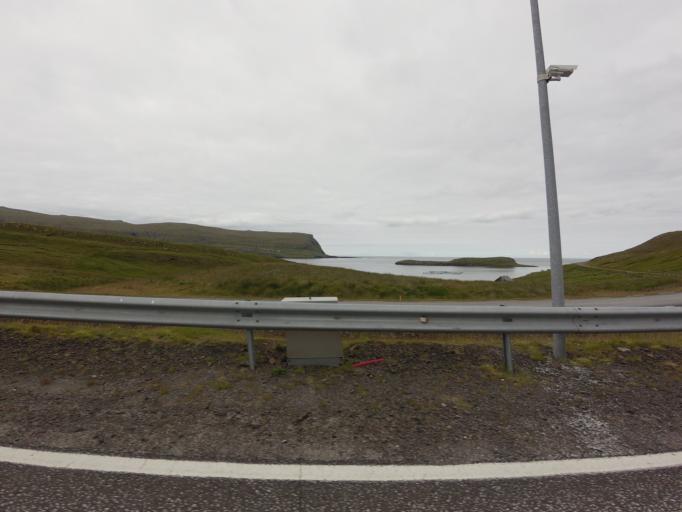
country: FO
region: Suduroy
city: Tvoroyri
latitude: 61.5295
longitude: -6.7951
